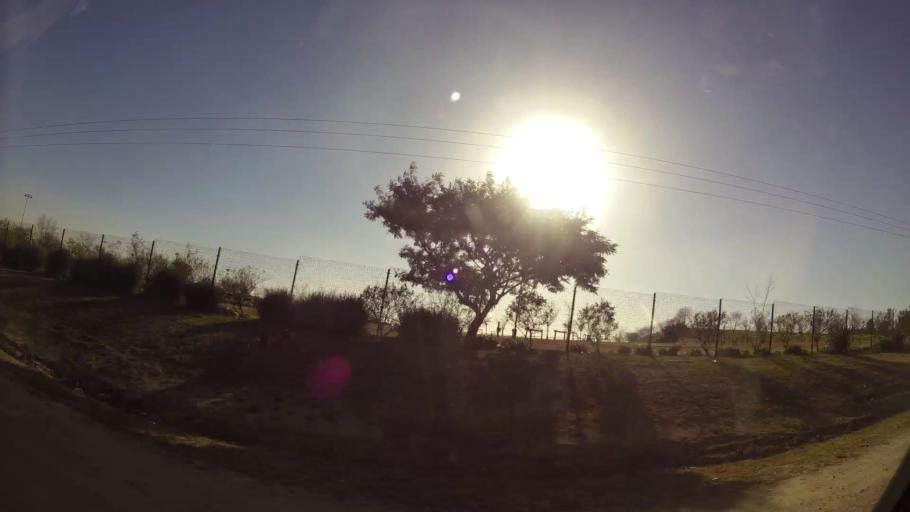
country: ZA
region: Gauteng
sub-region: City of Johannesburg Metropolitan Municipality
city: Diepsloot
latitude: -25.9510
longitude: 27.9647
